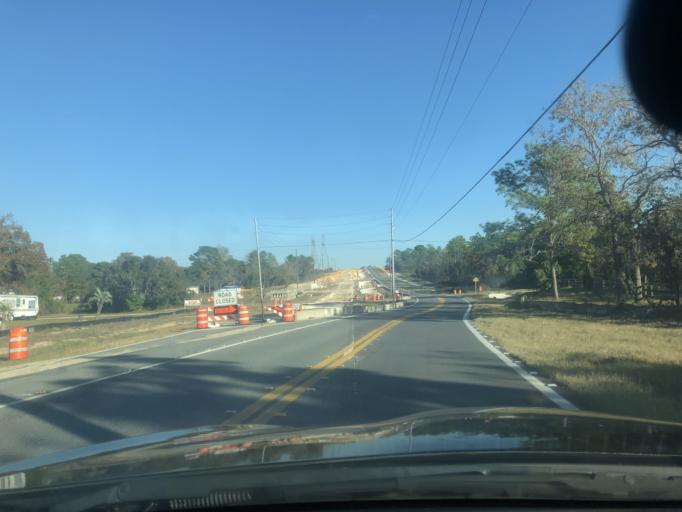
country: US
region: Florida
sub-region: Citrus County
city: Sugarmill Woods
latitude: 28.7640
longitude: -82.5069
